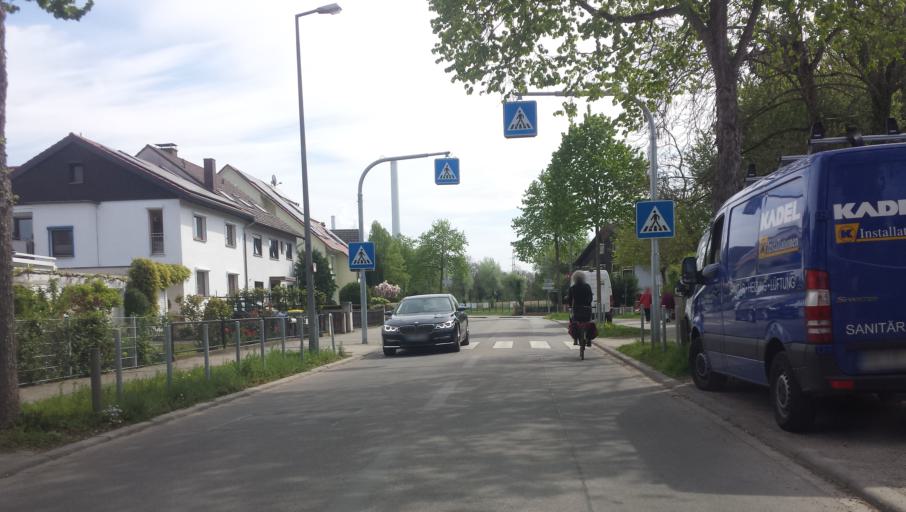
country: DE
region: Rheinland-Pfalz
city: Altrip
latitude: 49.4489
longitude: 8.4741
